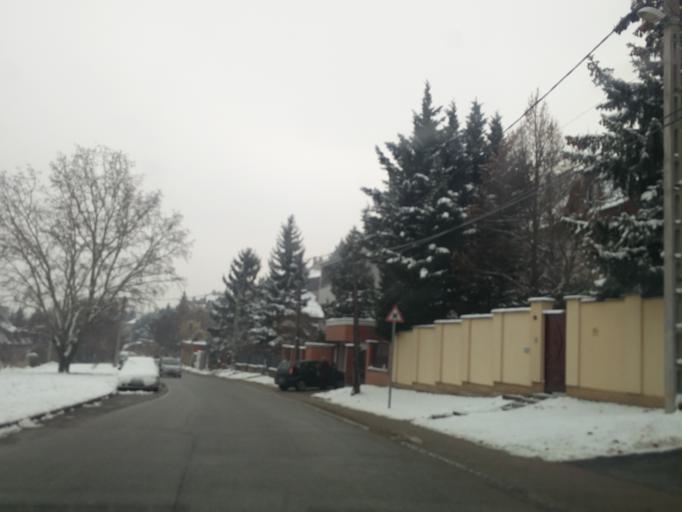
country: HU
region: Budapest
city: Budapest III. keruelet
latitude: 47.5398
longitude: 19.0215
